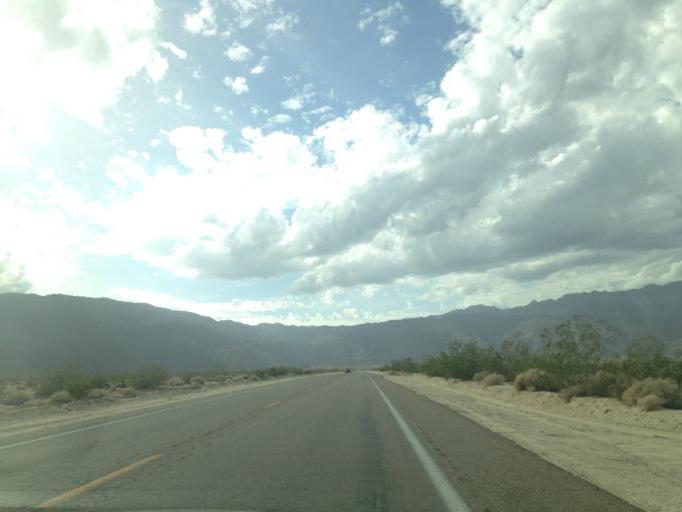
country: US
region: California
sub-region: San Diego County
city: Borrego Springs
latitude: 33.2114
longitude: -116.3505
